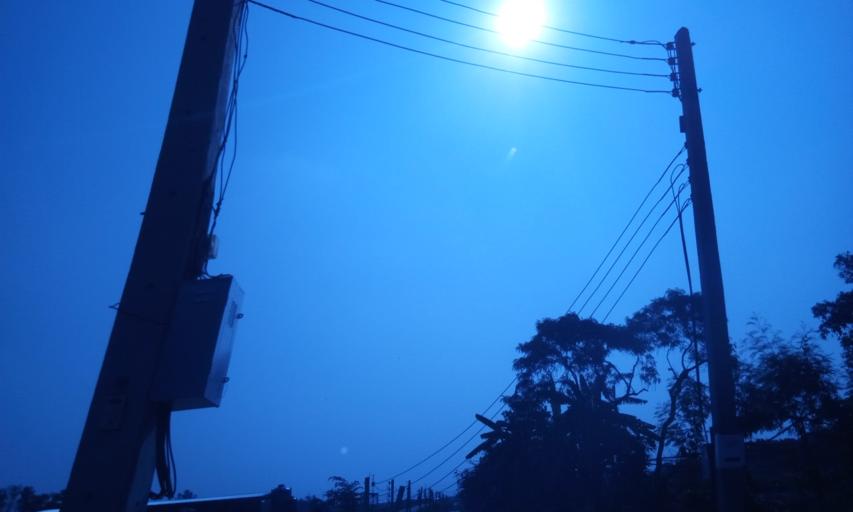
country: TH
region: Pathum Thani
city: Thanyaburi
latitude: 13.9775
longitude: 100.7061
